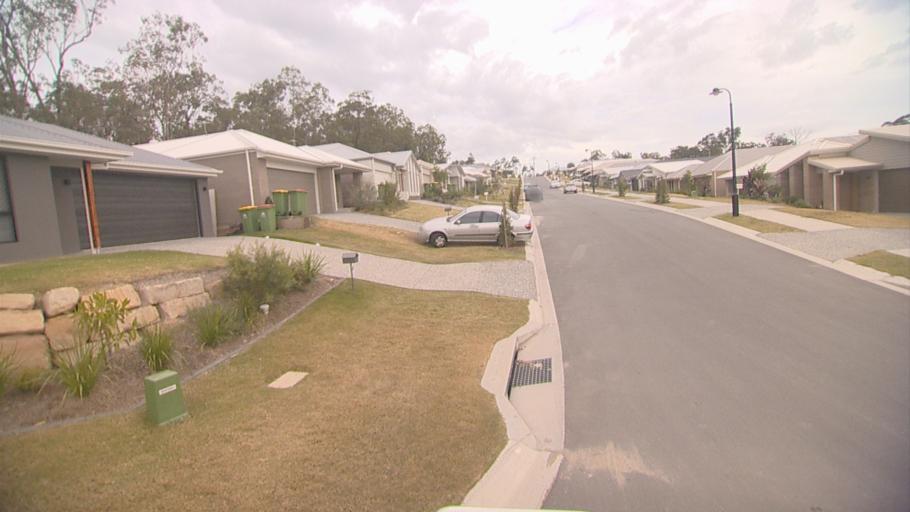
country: AU
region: Queensland
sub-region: Logan
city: Windaroo
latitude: -27.7236
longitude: 153.1648
